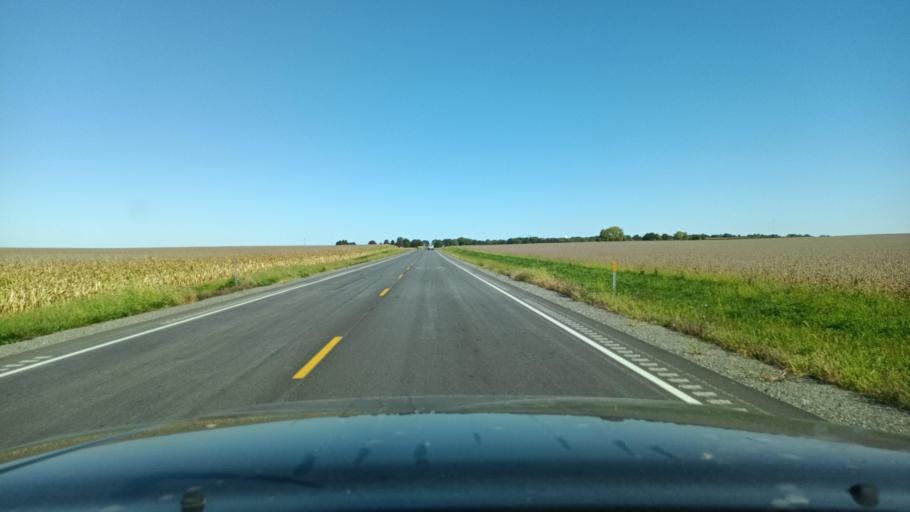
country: US
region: Illinois
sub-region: Champaign County
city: Philo
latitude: 39.9824
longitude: -88.1613
